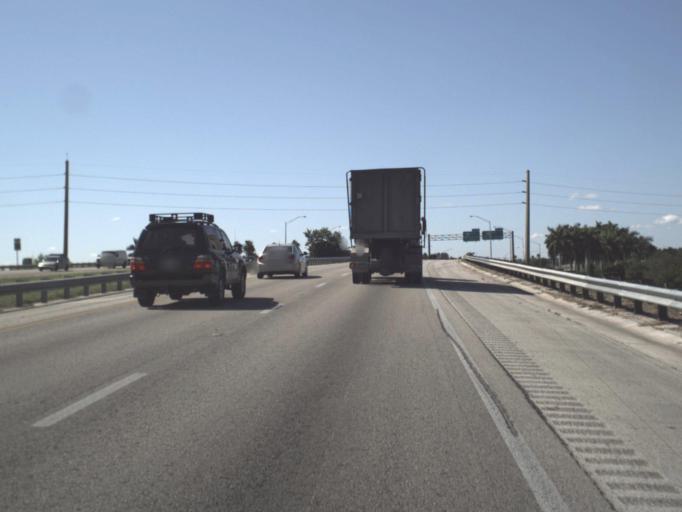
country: US
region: Florida
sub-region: Miami-Dade County
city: Goulds
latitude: 25.5388
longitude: -80.3650
